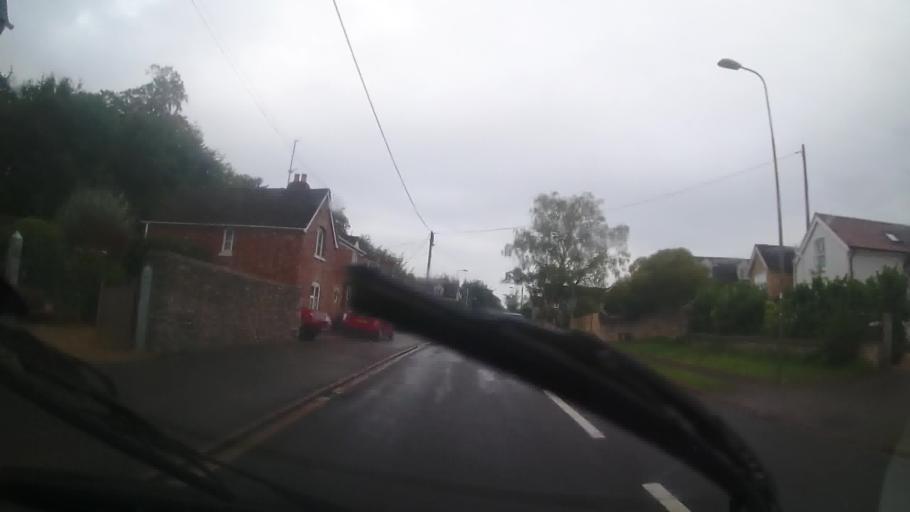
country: GB
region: England
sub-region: Oxfordshire
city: Woodstock
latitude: 51.8530
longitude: -1.3615
